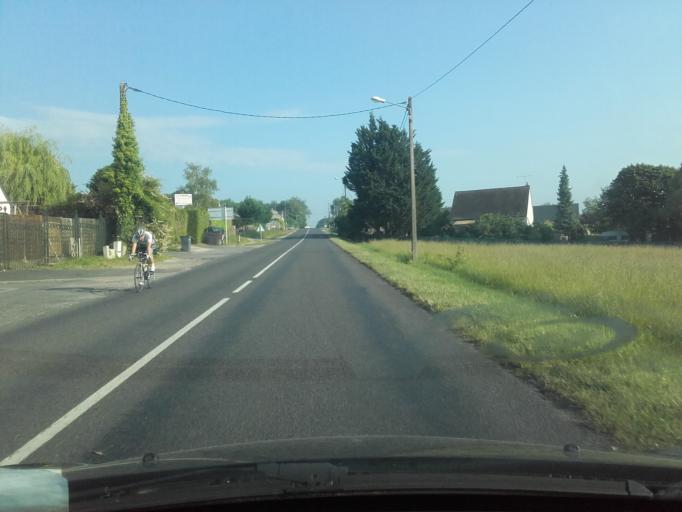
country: FR
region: Centre
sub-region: Departement d'Indre-et-Loire
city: Cinq-Mars-la-Pile
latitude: 47.3527
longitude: 0.4469
